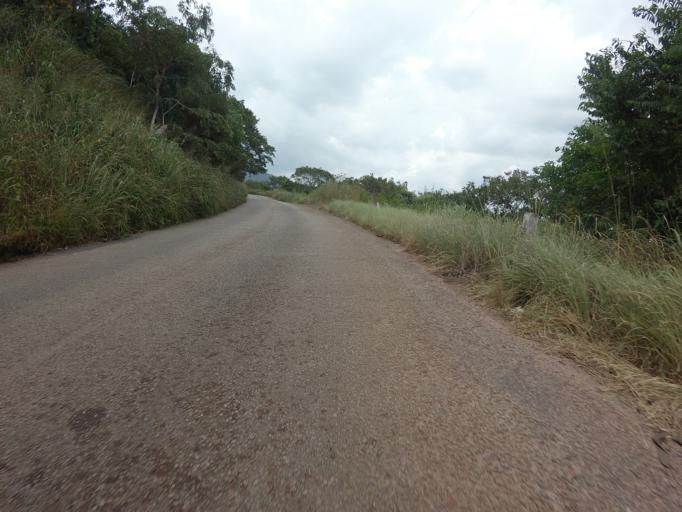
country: GH
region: Volta
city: Ho
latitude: 6.6788
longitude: 0.3530
